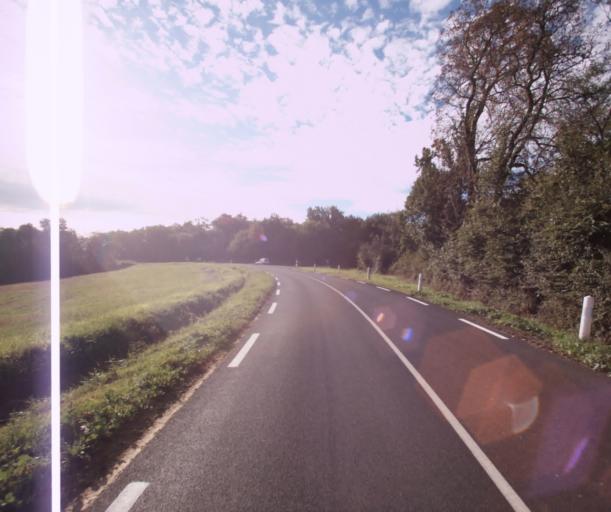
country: FR
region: Midi-Pyrenees
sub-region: Departement du Gers
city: Eauze
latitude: 43.8760
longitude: 0.0328
